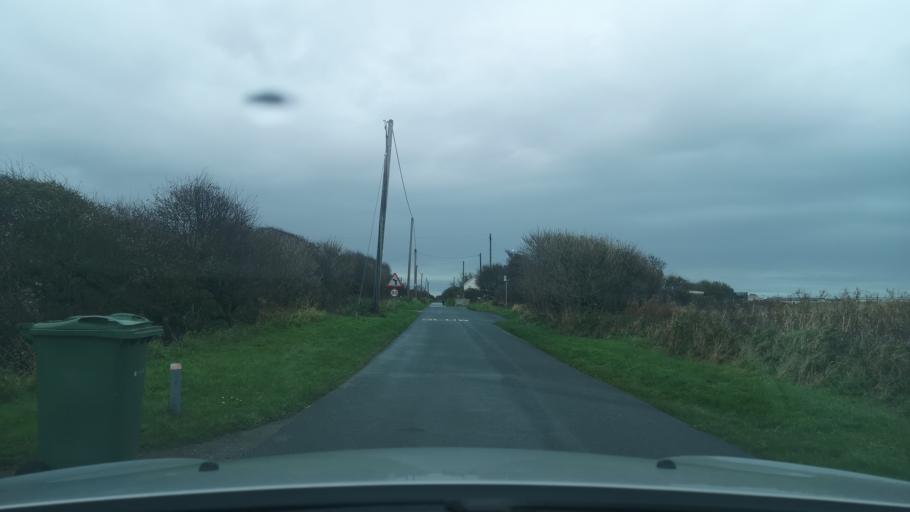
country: GB
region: England
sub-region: East Riding of Yorkshire
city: Easington
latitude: 53.6191
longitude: 0.1396
